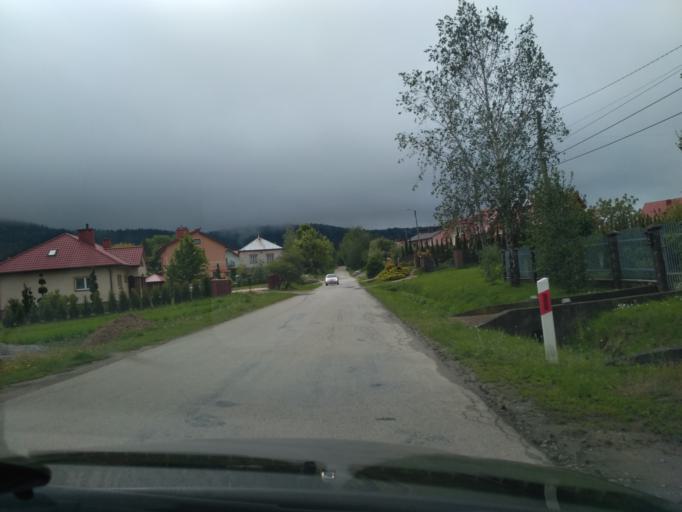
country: PL
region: Subcarpathian Voivodeship
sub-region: Powiat jasielski
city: Brzyska
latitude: 49.8242
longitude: 21.3739
